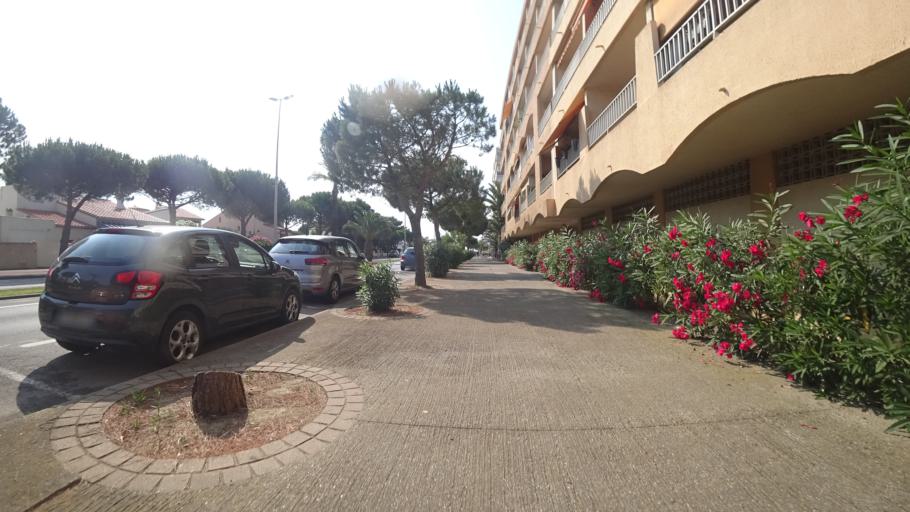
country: FR
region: Languedoc-Roussillon
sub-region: Departement des Pyrenees-Orientales
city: Saint-Cyprien-Plage
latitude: 42.6252
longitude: 3.0346
